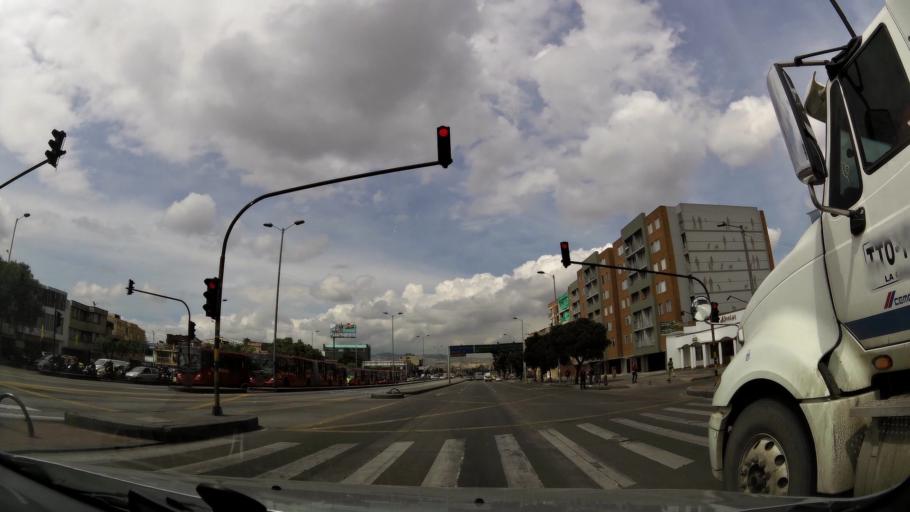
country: CO
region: Bogota D.C.
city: Bogota
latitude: 4.5998
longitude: -74.1054
